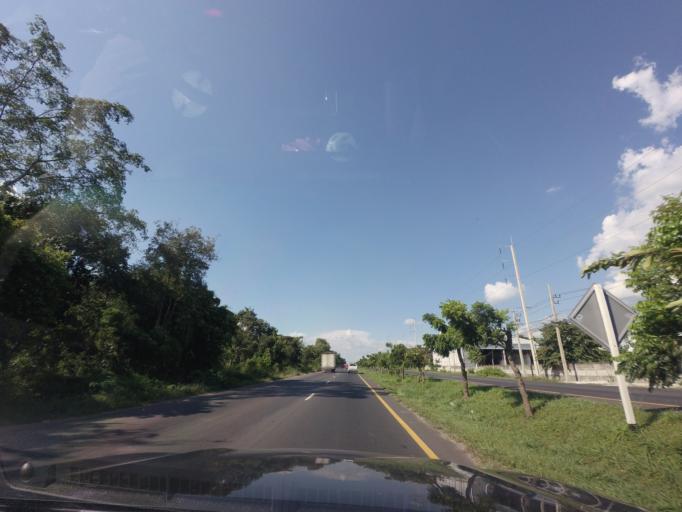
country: TH
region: Nakhon Ratchasima
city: Sida
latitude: 15.5531
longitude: 102.5494
